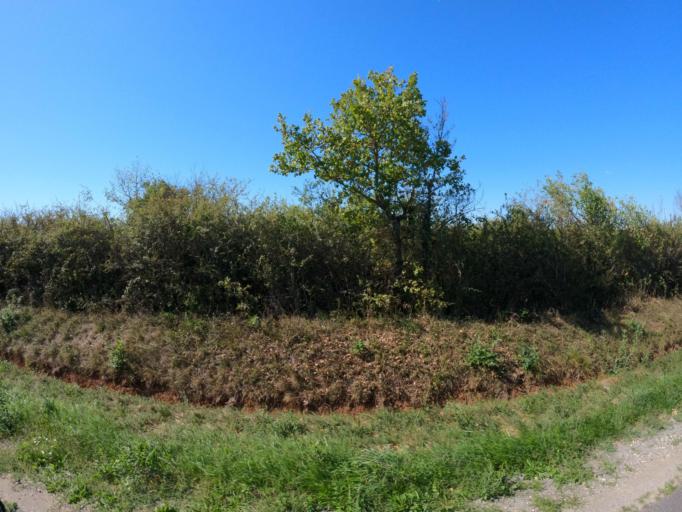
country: FR
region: Poitou-Charentes
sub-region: Departement de la Vienne
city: Lathus-Saint-Remy
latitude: 46.3625
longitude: 0.9410
